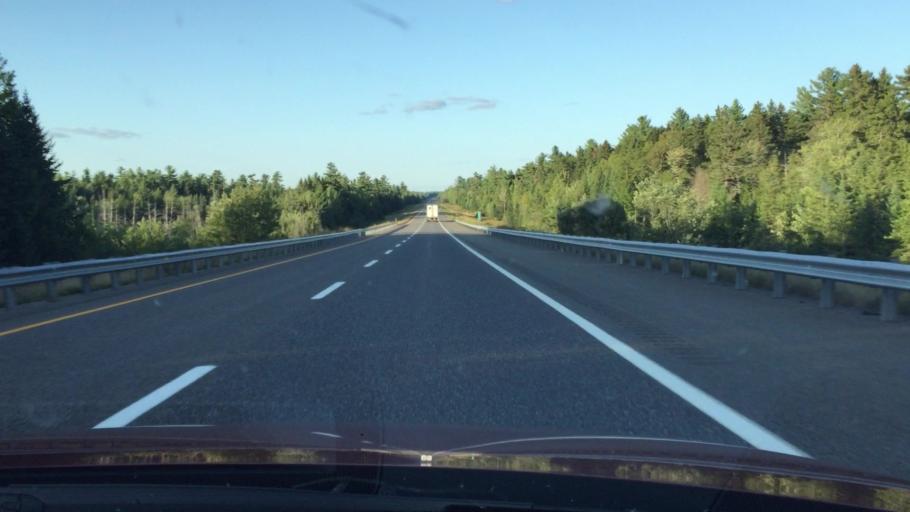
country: US
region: Maine
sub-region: Penobscot County
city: Patten
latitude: 46.0629
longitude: -68.2306
